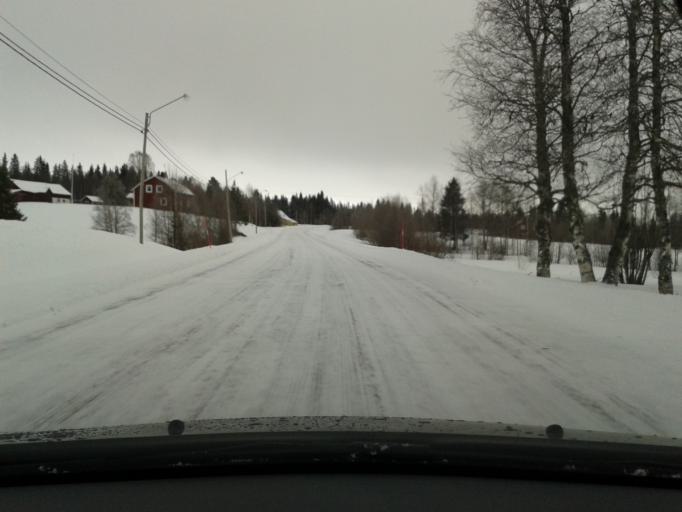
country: SE
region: Vaesterbotten
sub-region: Vilhelmina Kommun
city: Sjoberg
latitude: 64.8330
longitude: 15.9345
